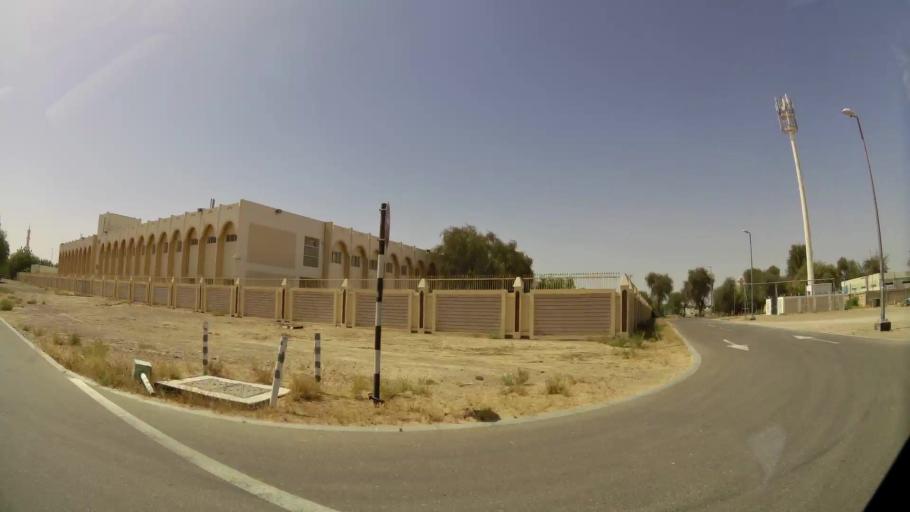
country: OM
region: Al Buraimi
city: Al Buraymi
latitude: 24.2895
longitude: 55.7652
